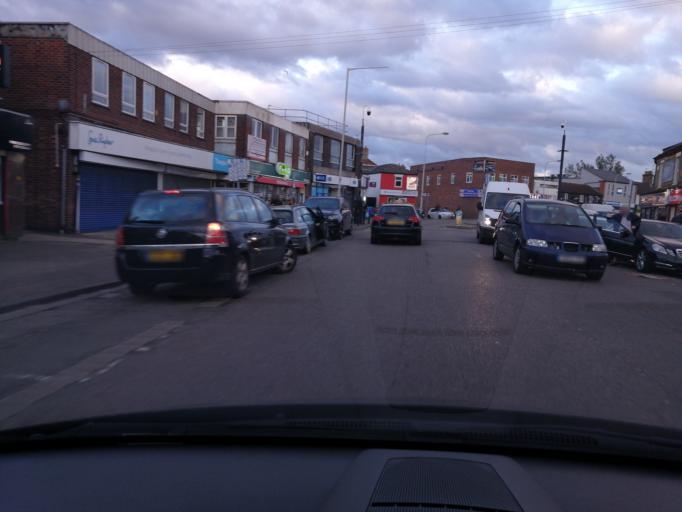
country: GB
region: England
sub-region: Peterborough
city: Peterborough
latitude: 52.5880
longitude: -0.2472
